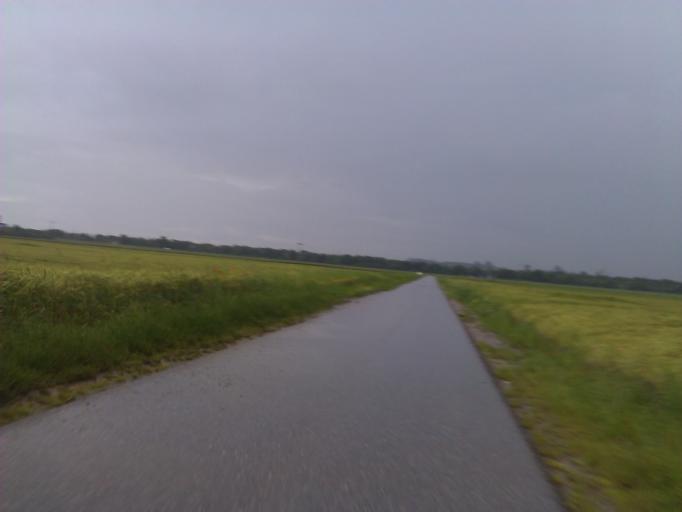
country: DE
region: Bavaria
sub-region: Swabia
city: Bad Worishofen
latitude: 48.0495
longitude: 10.5855
